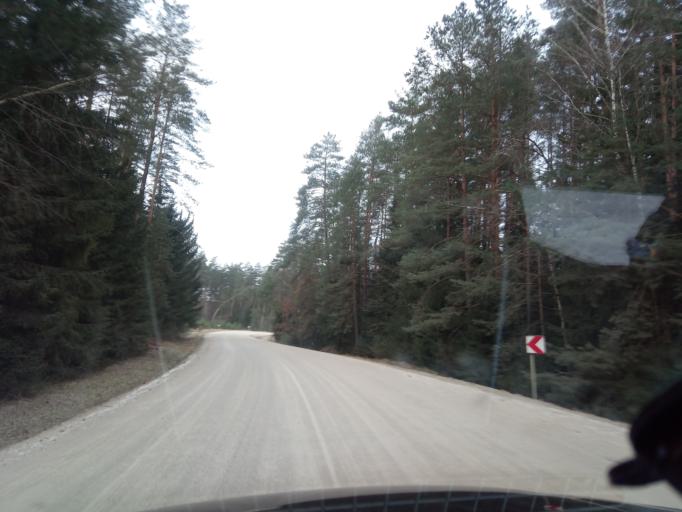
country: LT
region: Alytaus apskritis
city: Varena
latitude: 54.1481
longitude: 24.6029
